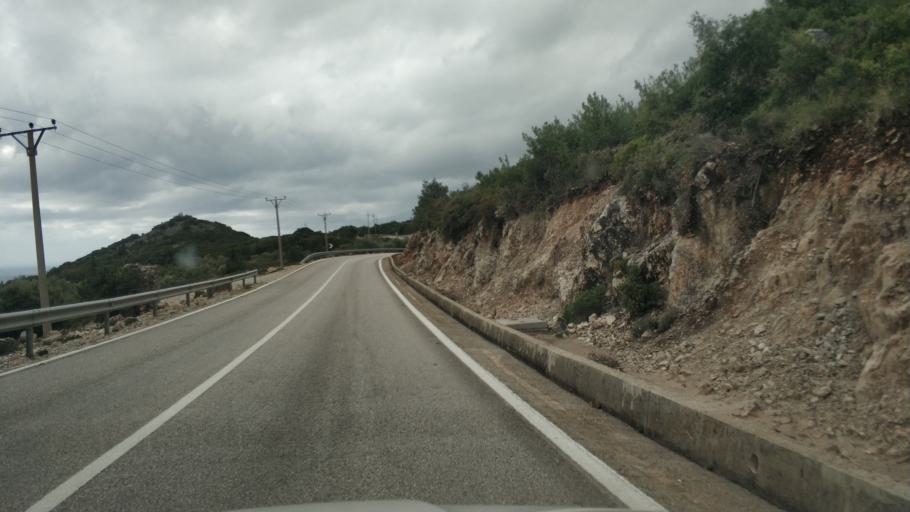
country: AL
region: Vlore
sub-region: Rrethi i Vlores
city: Vranisht
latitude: 40.1419
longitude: 19.6681
